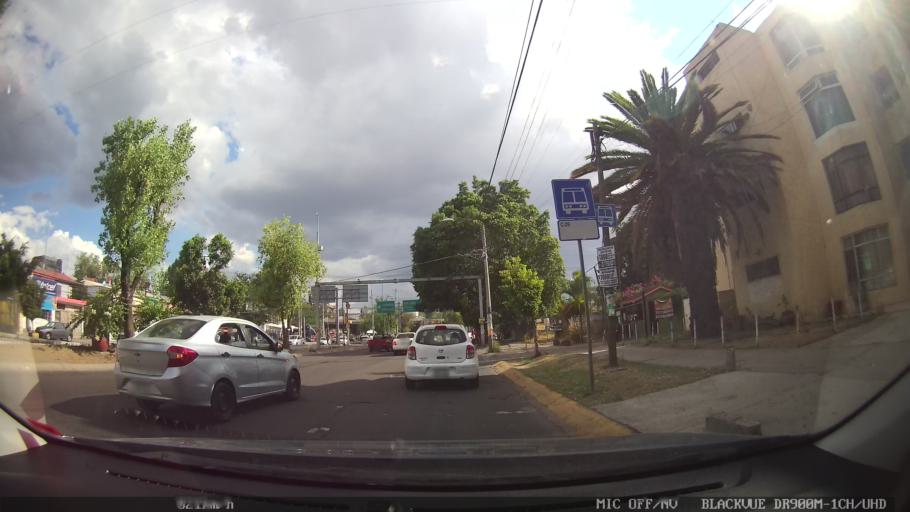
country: MX
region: Jalisco
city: Tlaquepaque
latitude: 20.6283
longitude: -103.2859
